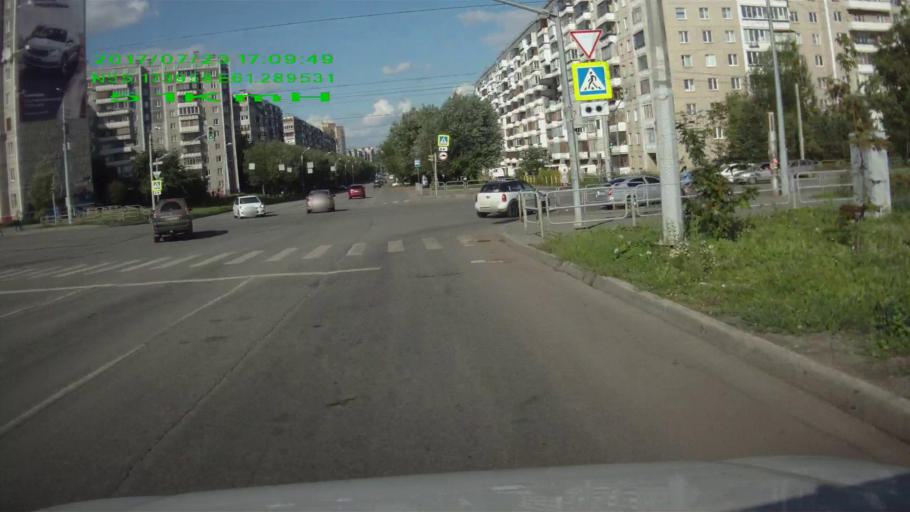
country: RU
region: Chelyabinsk
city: Roshchino
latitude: 55.1742
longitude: 61.2903
